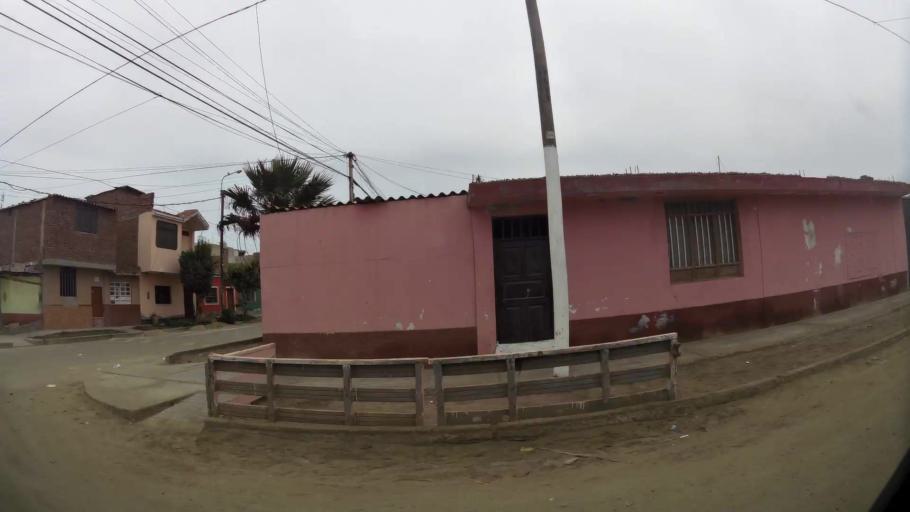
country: PE
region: La Libertad
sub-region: Provincia de Trujillo
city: Buenos Aires
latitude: -8.1468
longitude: -79.0501
